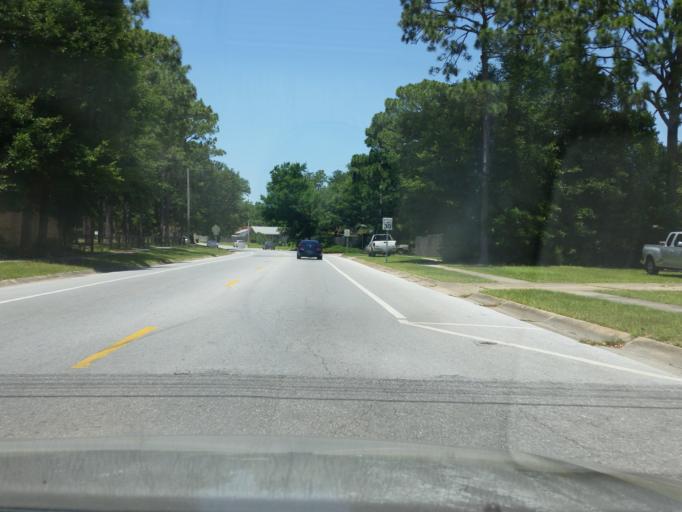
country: US
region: Florida
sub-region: Escambia County
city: Ferry Pass
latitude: 30.4878
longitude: -87.1793
